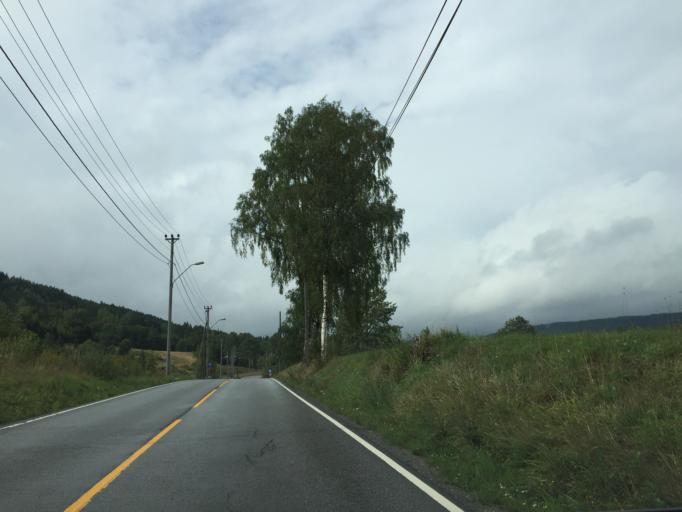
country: NO
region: Akershus
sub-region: Baerum
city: Lysaker
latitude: 60.0179
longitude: 10.5928
